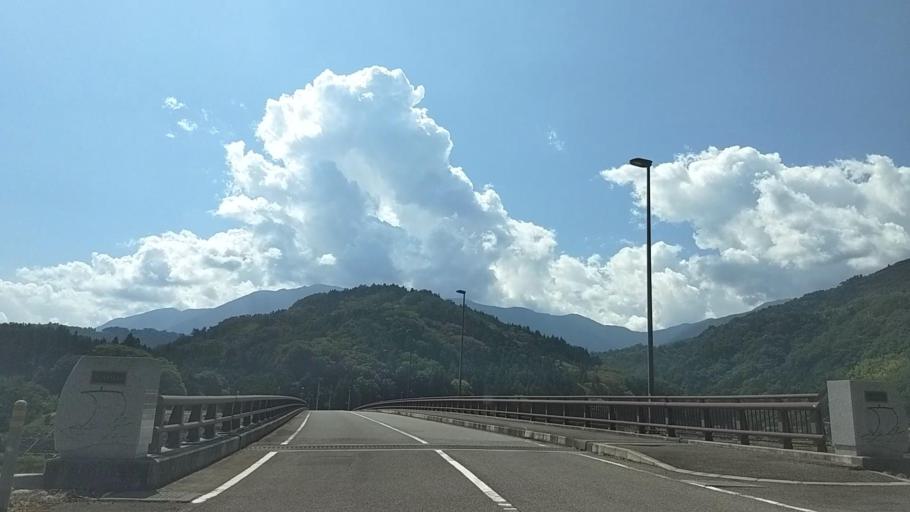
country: JP
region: Yamanashi
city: Ryuo
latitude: 35.5130
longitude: 138.4596
